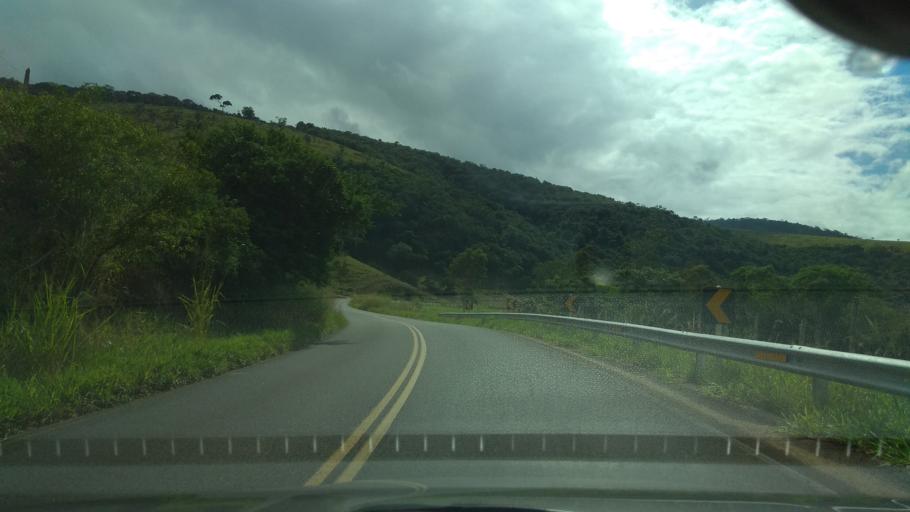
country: BR
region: Bahia
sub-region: Ubaira
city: Ubaira
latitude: -13.2620
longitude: -39.7051
